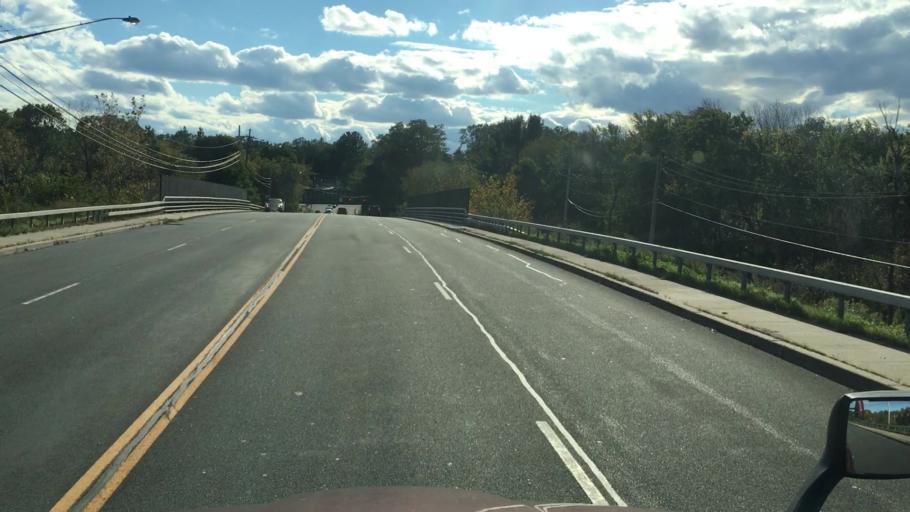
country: US
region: New York
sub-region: Schenectady County
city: Scotia
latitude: 42.8360
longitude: -73.9546
